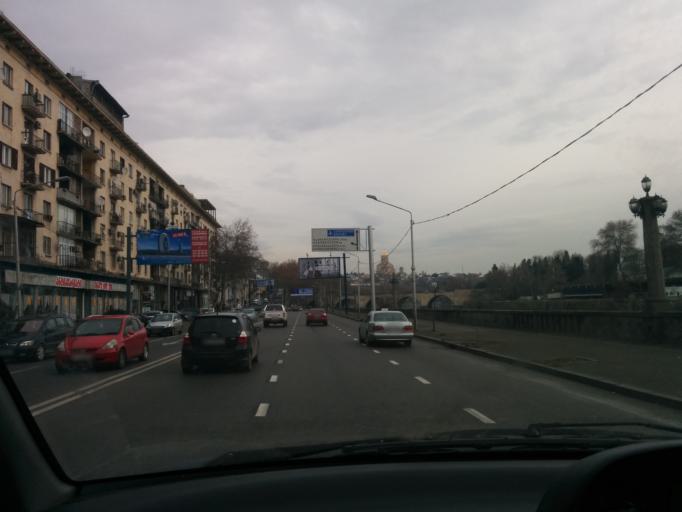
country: GE
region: T'bilisi
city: Tbilisi
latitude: 41.7037
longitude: 44.7992
